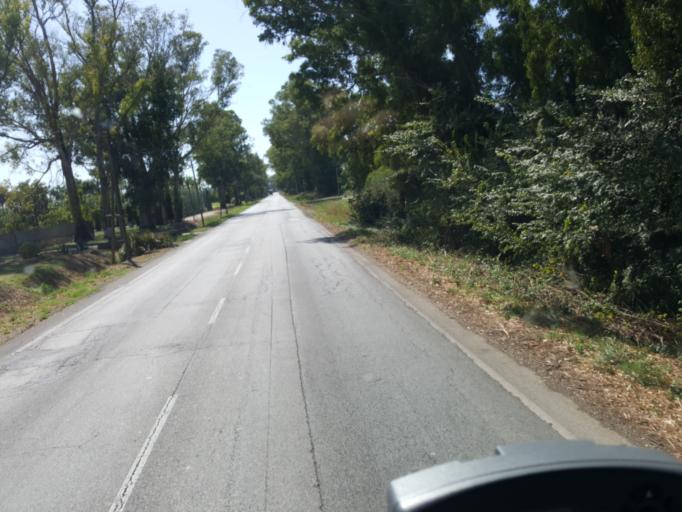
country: IT
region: Latium
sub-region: Provincia di Latina
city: Borgo Hermada
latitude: 41.3591
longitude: 13.1082
